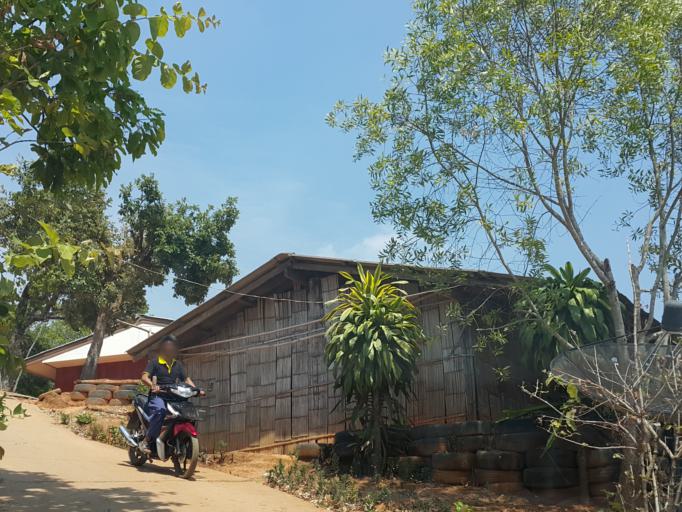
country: TH
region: Chiang Mai
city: Samoeng
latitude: 18.8849
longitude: 98.7842
